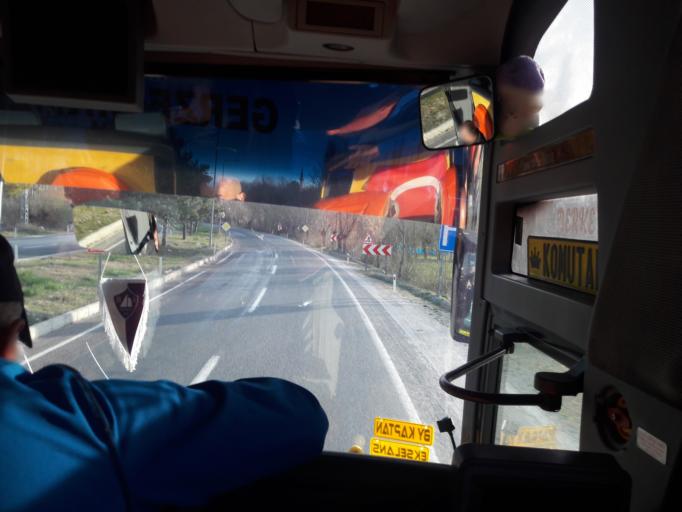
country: TR
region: Cankiri
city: Korgun
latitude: 40.7378
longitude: 33.5206
